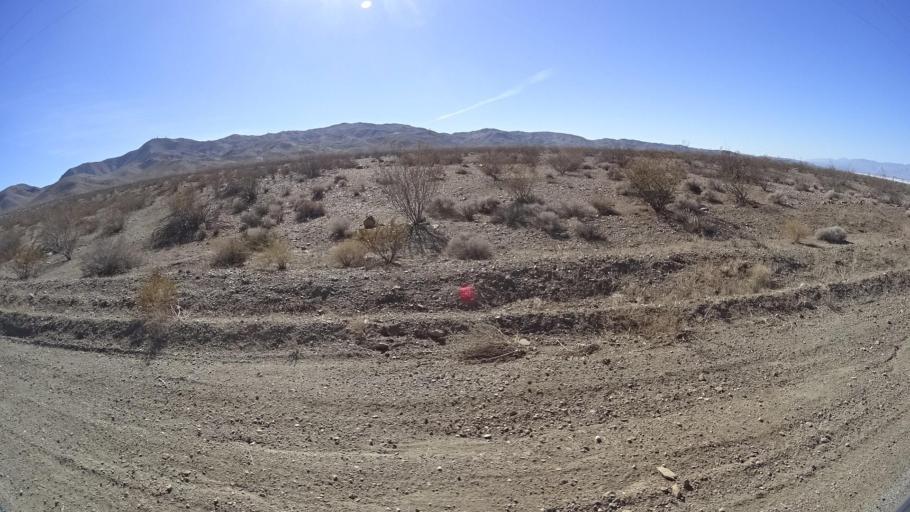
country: US
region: California
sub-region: Kern County
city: Ridgecrest
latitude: 35.3823
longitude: -117.6959
